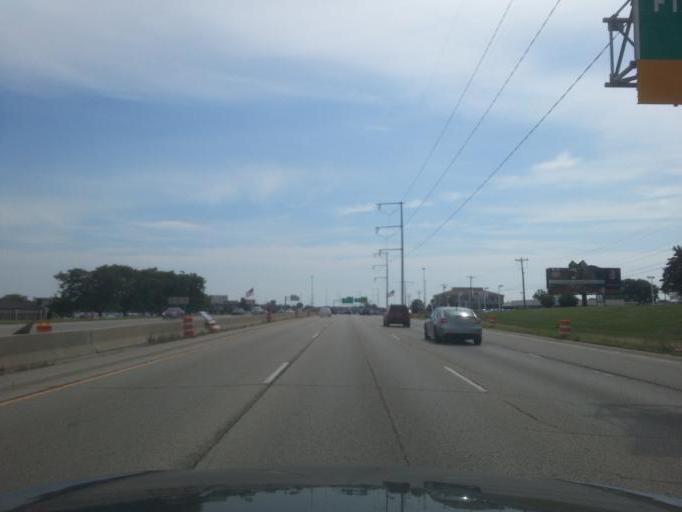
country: US
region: Wisconsin
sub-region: Dane County
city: Madison
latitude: 43.0349
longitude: -89.4139
